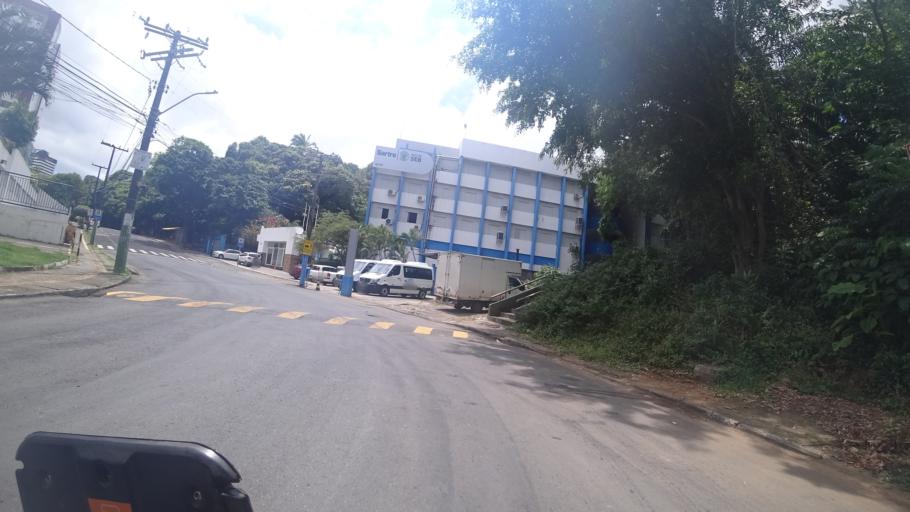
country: BR
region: Bahia
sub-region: Salvador
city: Salvador
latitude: -12.9942
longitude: -38.4709
